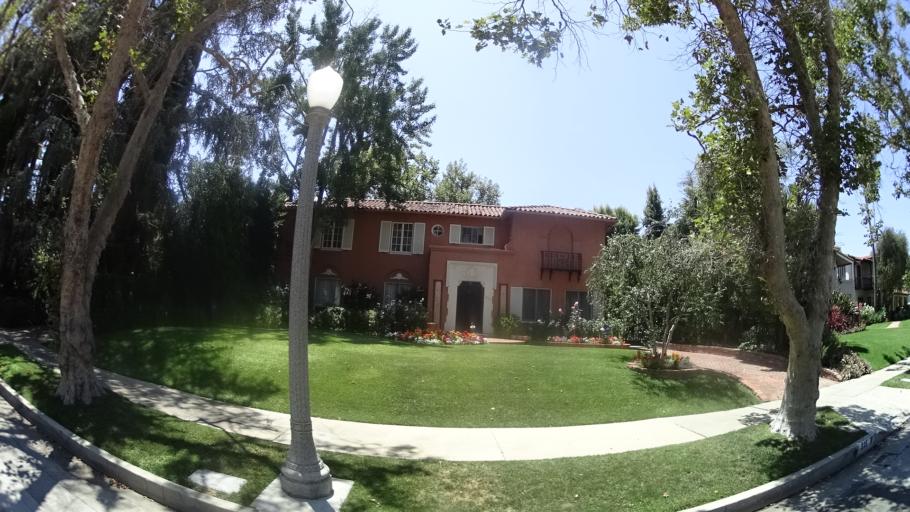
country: US
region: California
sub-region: Los Angeles County
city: Hollywood
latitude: 34.0768
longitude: -118.3372
